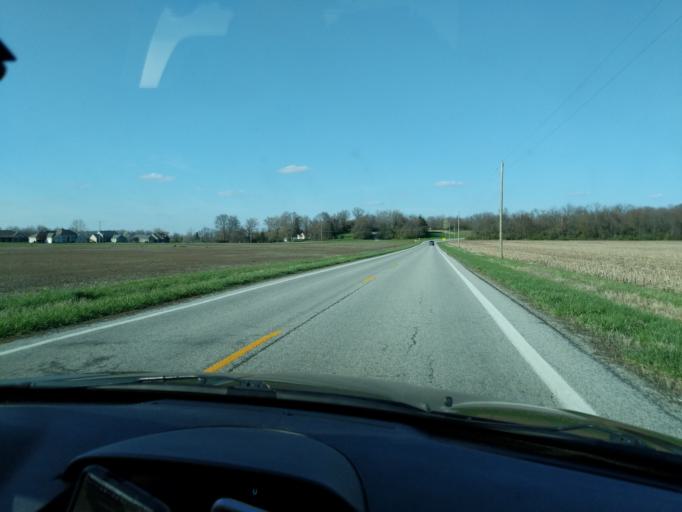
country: US
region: Ohio
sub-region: Champaign County
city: Urbana
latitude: 40.0827
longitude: -83.7966
